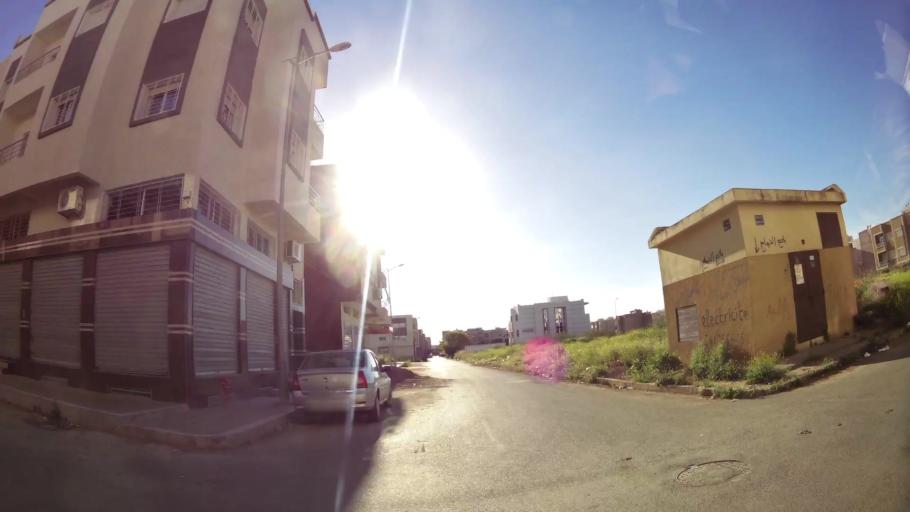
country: MA
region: Fes-Boulemane
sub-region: Fes
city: Fes
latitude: 34.0087
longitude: -5.0139
